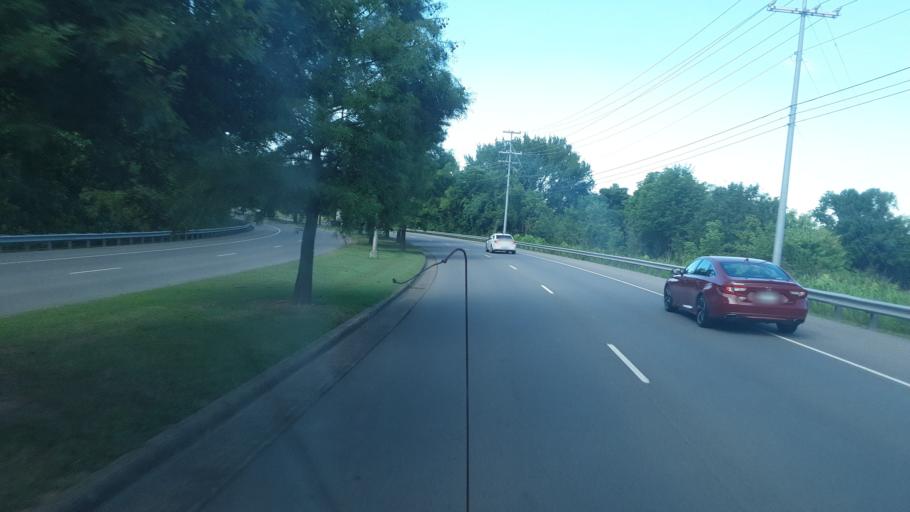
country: US
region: Tennessee
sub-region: Montgomery County
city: Clarksville
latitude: 36.5758
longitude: -87.2835
